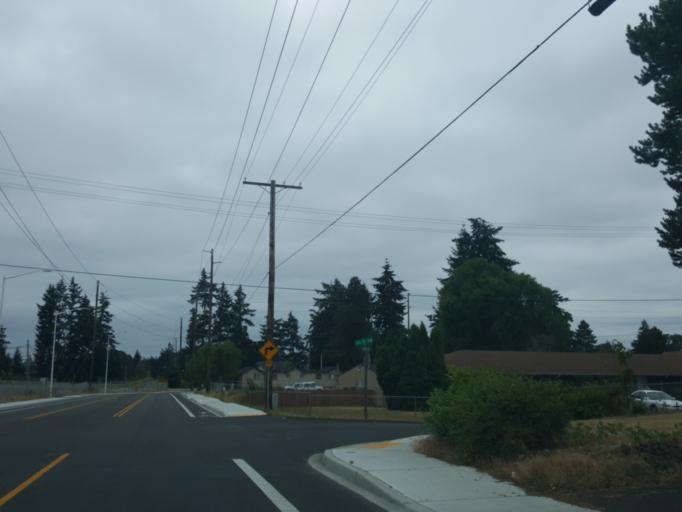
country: US
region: Washington
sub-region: Pierce County
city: McChord Air Force Base
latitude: 47.1577
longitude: -122.4957
